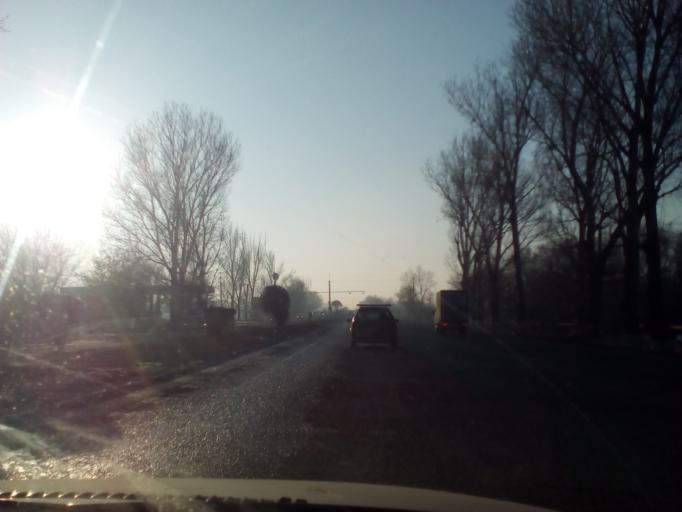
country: KZ
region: Almaty Oblysy
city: Burunday
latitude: 43.2238
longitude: 76.6032
